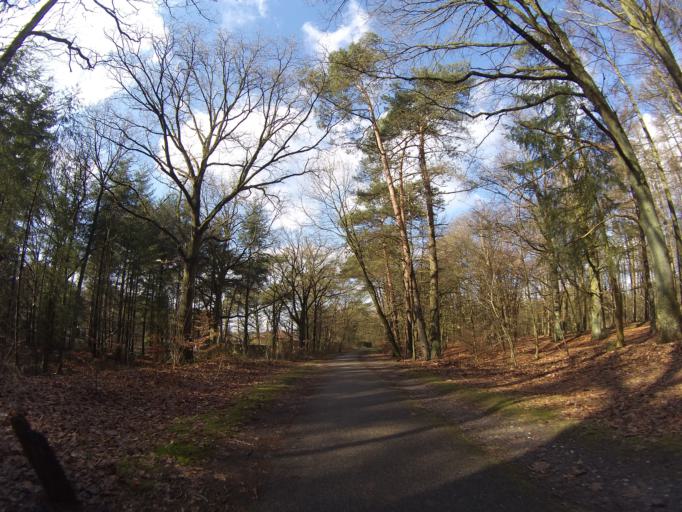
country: NL
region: Utrecht
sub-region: Gemeente Zeist
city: Zeist
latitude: 52.1245
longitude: 5.2191
